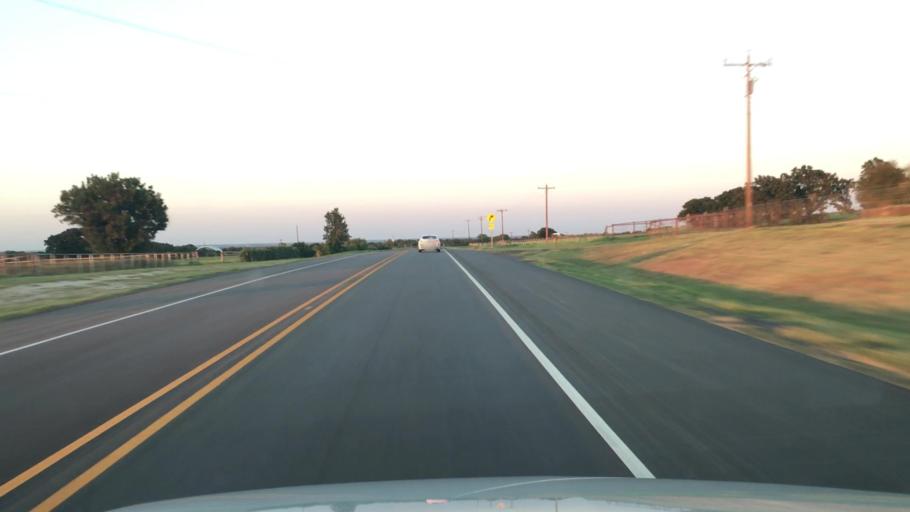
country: US
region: Texas
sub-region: Somervell County
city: Glen Rose
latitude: 32.1911
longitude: -97.8531
